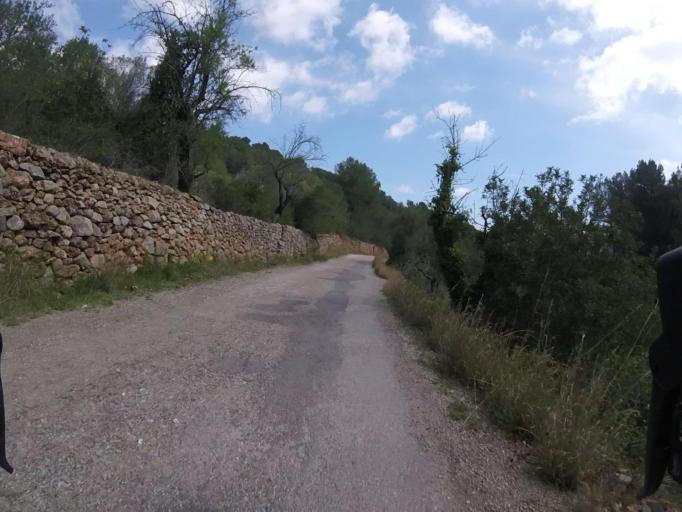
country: ES
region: Valencia
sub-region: Provincia de Castello
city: Cabanes
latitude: 40.1118
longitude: 0.0440
